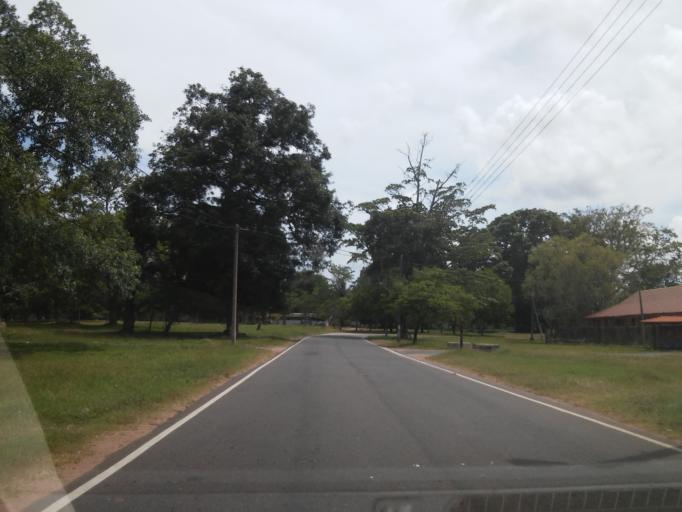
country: LK
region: North Central
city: Anuradhapura
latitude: 8.3472
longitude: 80.4009
